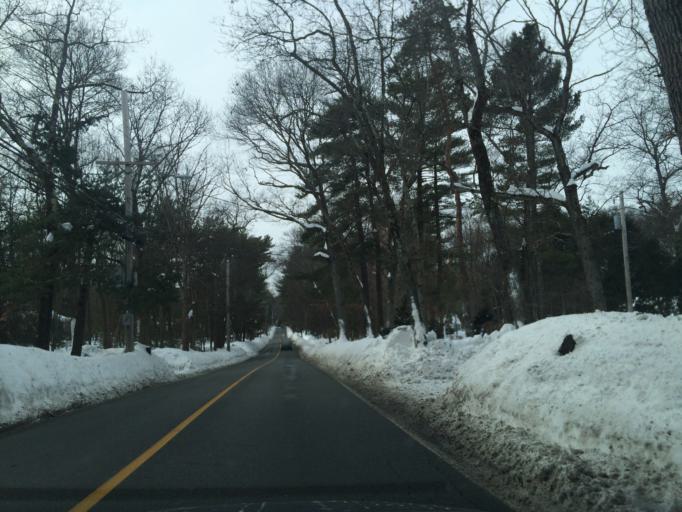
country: US
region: Massachusetts
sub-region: Norfolk County
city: Wellesley
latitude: 42.3240
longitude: -71.3121
